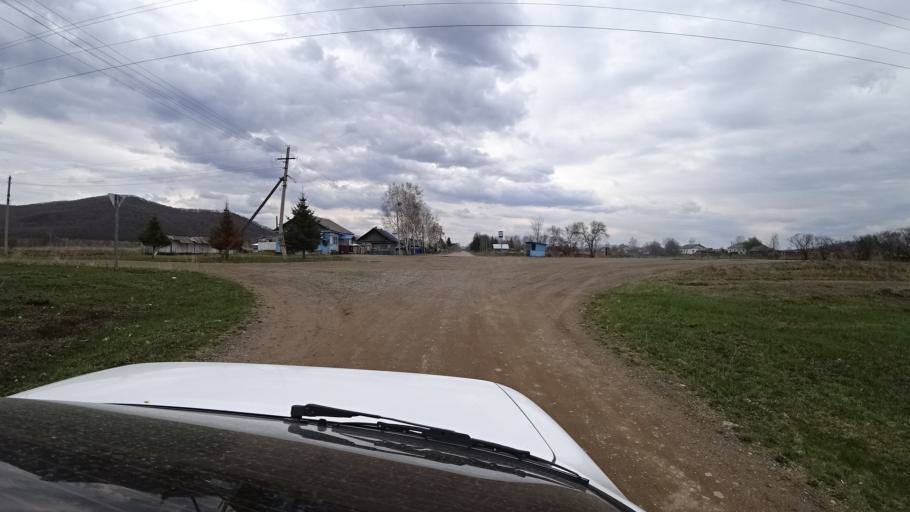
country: RU
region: Primorskiy
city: Novopokrovka
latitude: 45.5783
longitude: 134.3124
